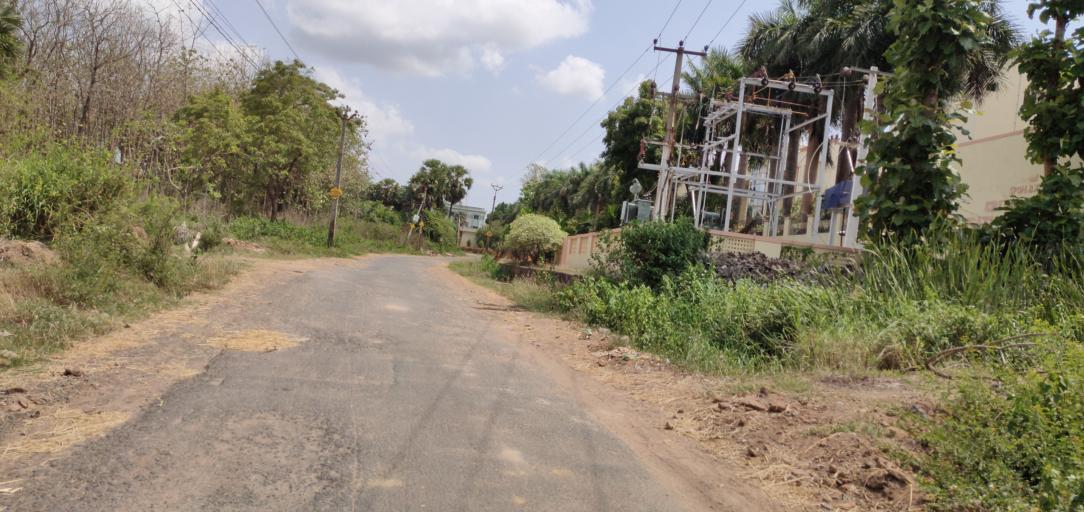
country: IN
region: Andhra Pradesh
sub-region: West Godavari
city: Tadepallegudem
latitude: 16.8573
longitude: 81.4941
